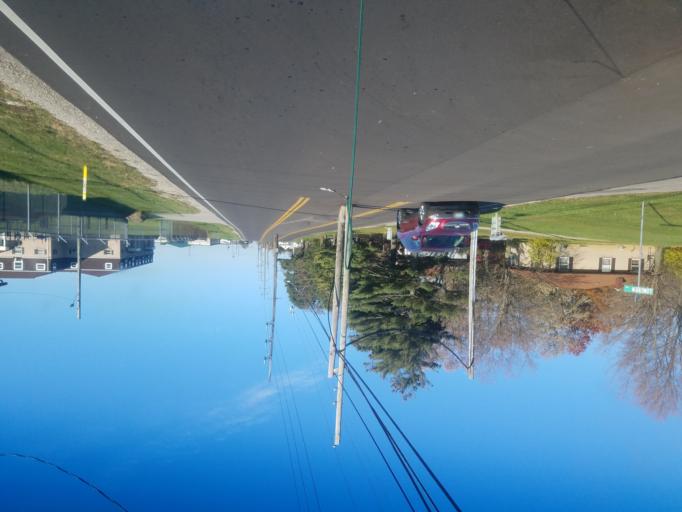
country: US
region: Ohio
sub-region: Richland County
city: Ontario
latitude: 40.7763
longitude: -82.5558
